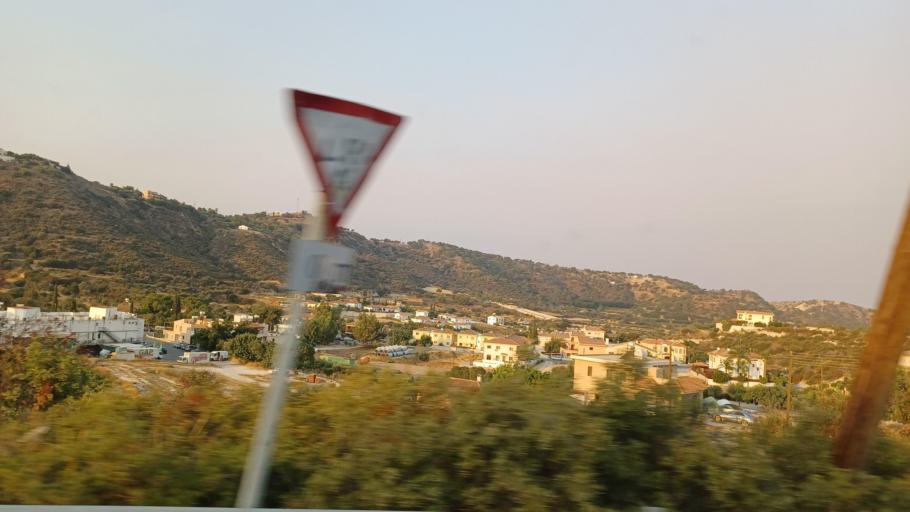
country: CY
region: Limassol
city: Pissouri
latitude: 34.6773
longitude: 32.6973
